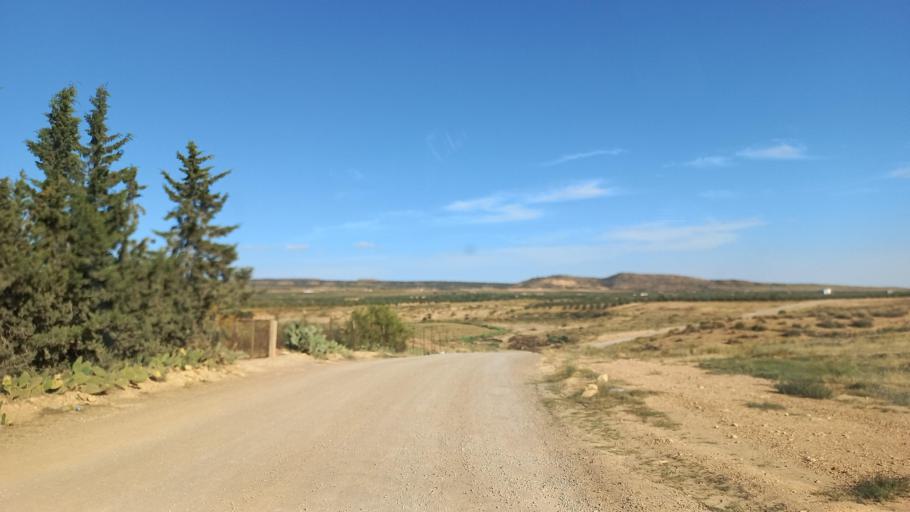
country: TN
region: Al Qasrayn
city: Sbiba
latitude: 35.3020
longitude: 9.0931
